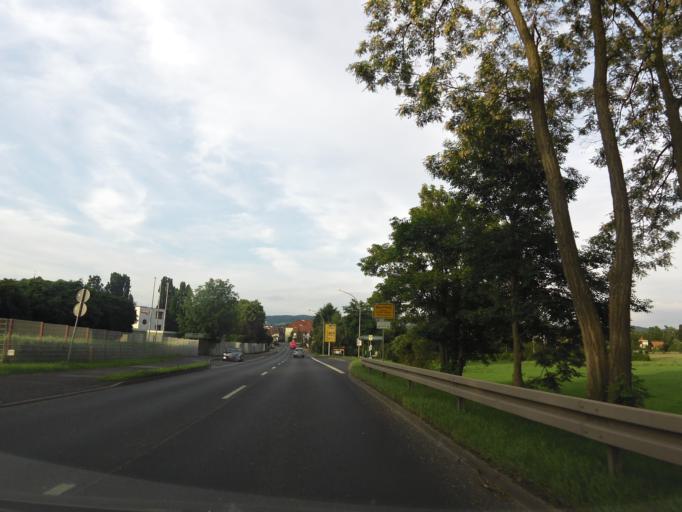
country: DE
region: Thuringia
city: Barchfeld
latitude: 50.7980
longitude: 10.2946
